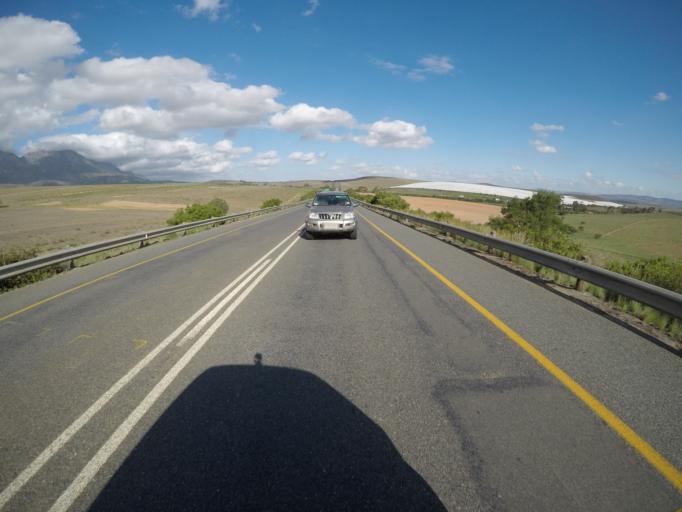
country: ZA
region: Western Cape
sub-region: Overberg District Municipality
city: Swellendam
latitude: -33.9566
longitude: 20.2354
